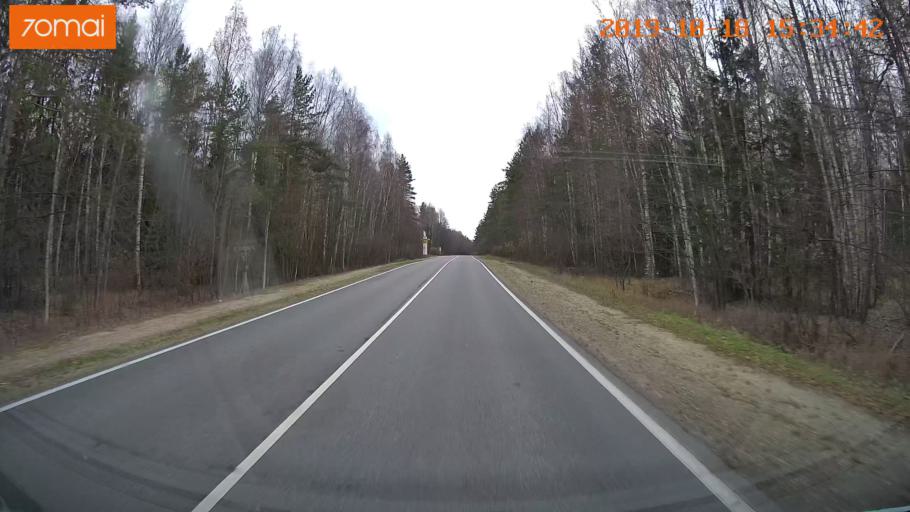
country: RU
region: Vladimir
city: Anopino
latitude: 55.8576
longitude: 40.6387
